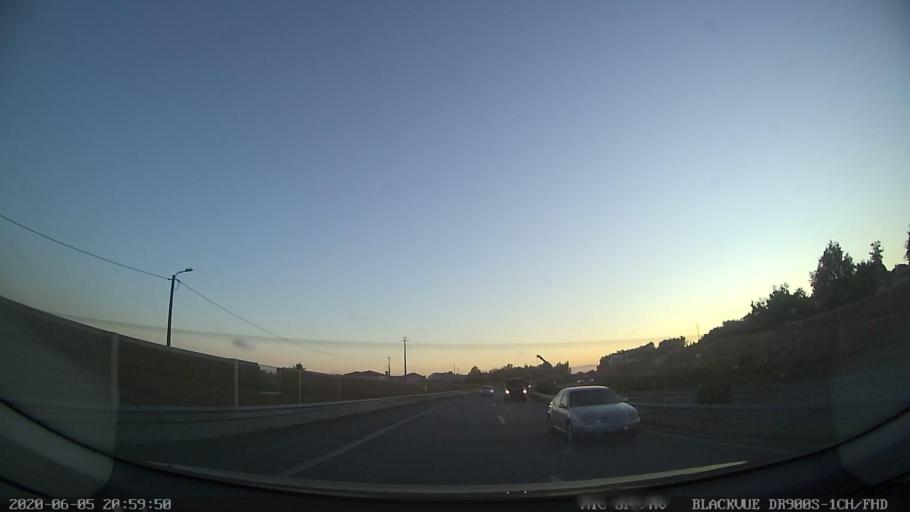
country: PT
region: Porto
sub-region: Lousada
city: Meinedo
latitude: 41.2189
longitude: -8.2423
